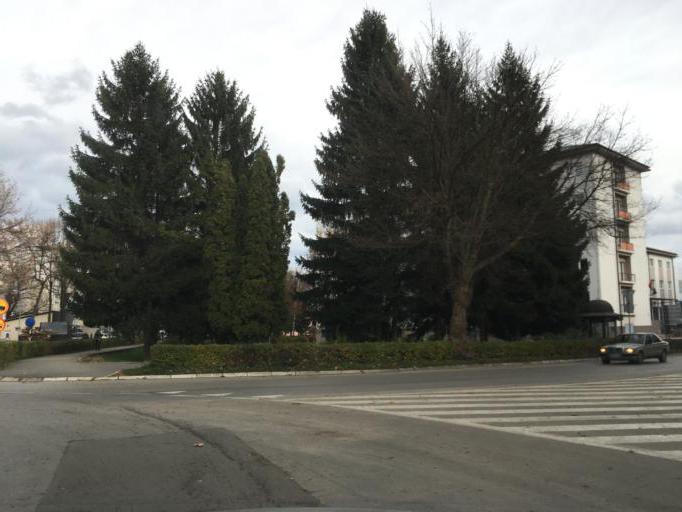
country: BA
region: Federation of Bosnia and Herzegovina
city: Bugojno
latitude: 44.0509
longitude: 17.4379
